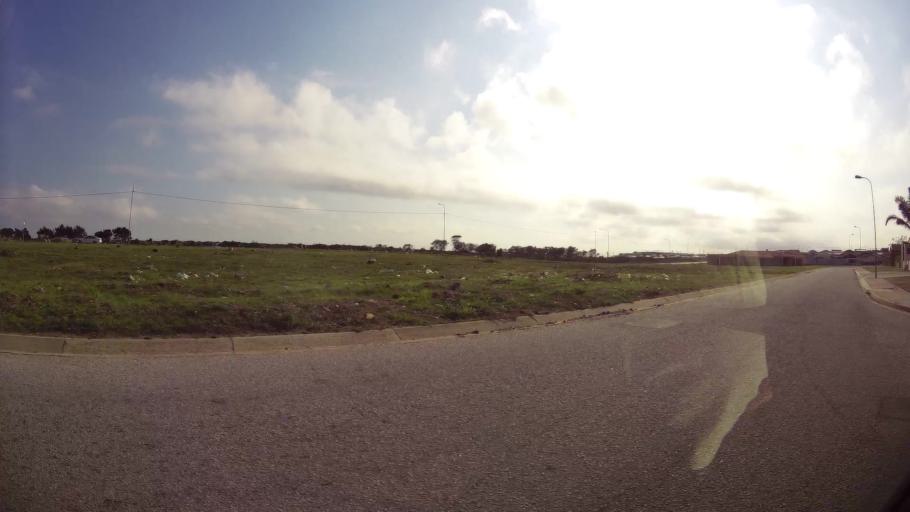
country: ZA
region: Eastern Cape
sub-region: Nelson Mandela Bay Metropolitan Municipality
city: Port Elizabeth
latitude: -33.9183
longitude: 25.5317
